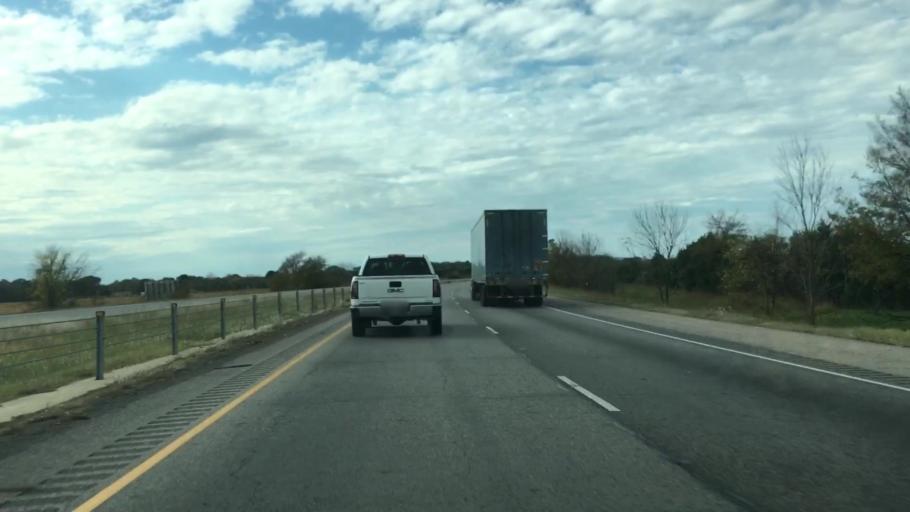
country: US
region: Arkansas
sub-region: Conway County
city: Morrilton
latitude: 35.1950
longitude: -92.7978
